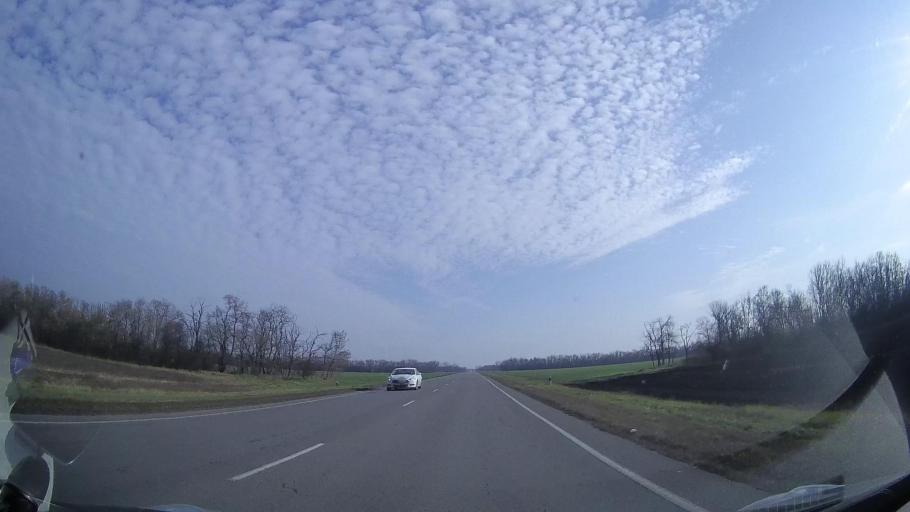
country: RU
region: Rostov
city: Tselina
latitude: 46.5243
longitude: 41.1099
